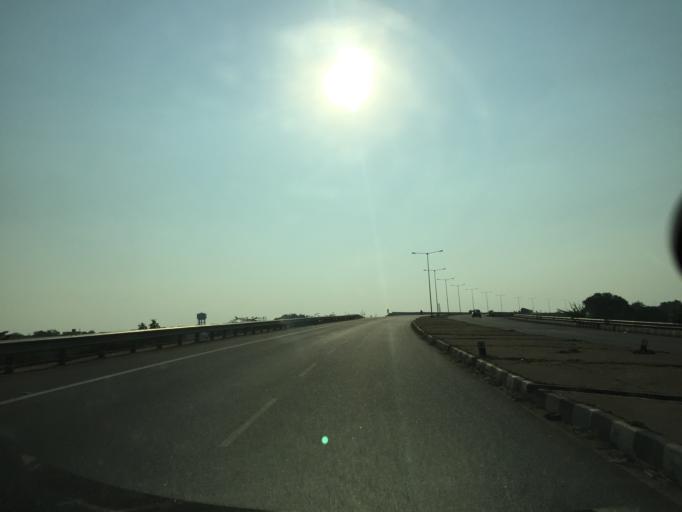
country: IN
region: Telangana
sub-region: Nalgonda
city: Bhongir
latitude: 17.5012
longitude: 78.8937
